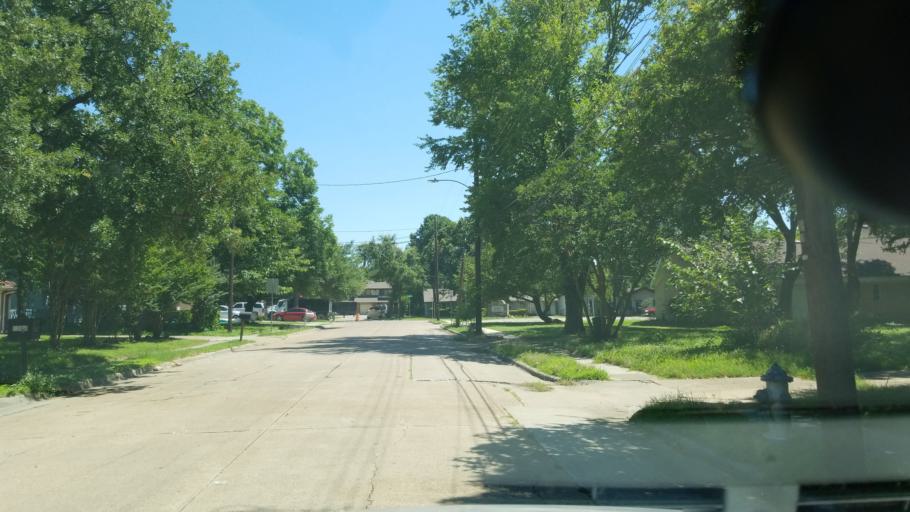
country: US
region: Texas
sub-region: Dallas County
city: Irving
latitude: 32.8277
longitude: -96.9377
